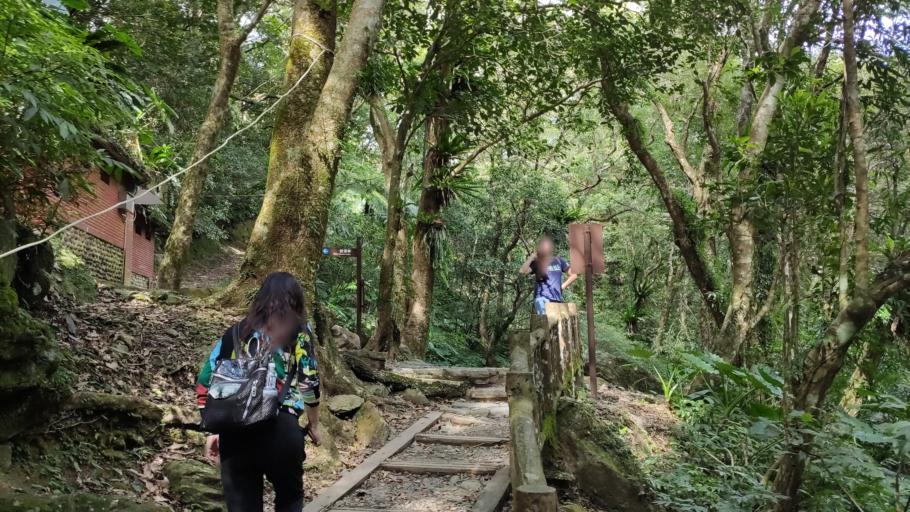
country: TW
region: Taiwan
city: Daxi
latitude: 24.8183
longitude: 121.4499
